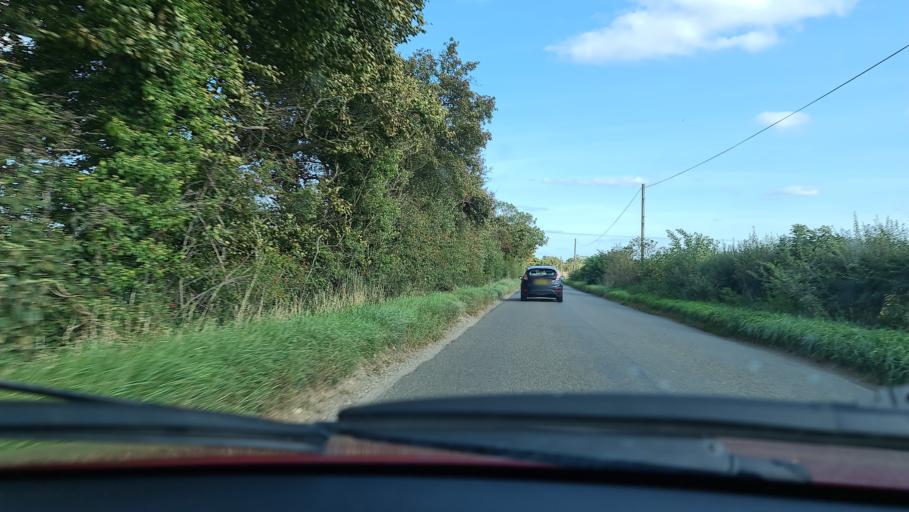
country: GB
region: England
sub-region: Northamptonshire
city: Brackley
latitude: 52.0133
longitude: -1.1631
